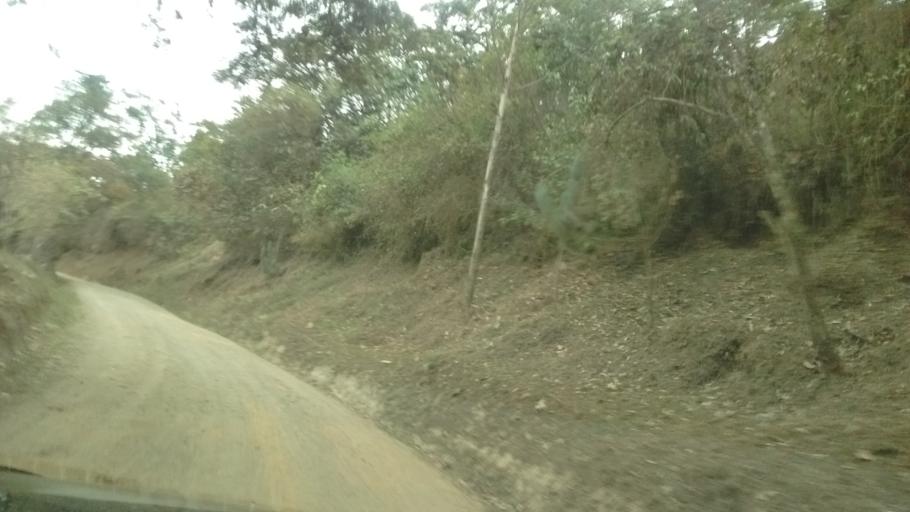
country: CO
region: Cauca
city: La Vega
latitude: 2.0113
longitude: -76.7931
